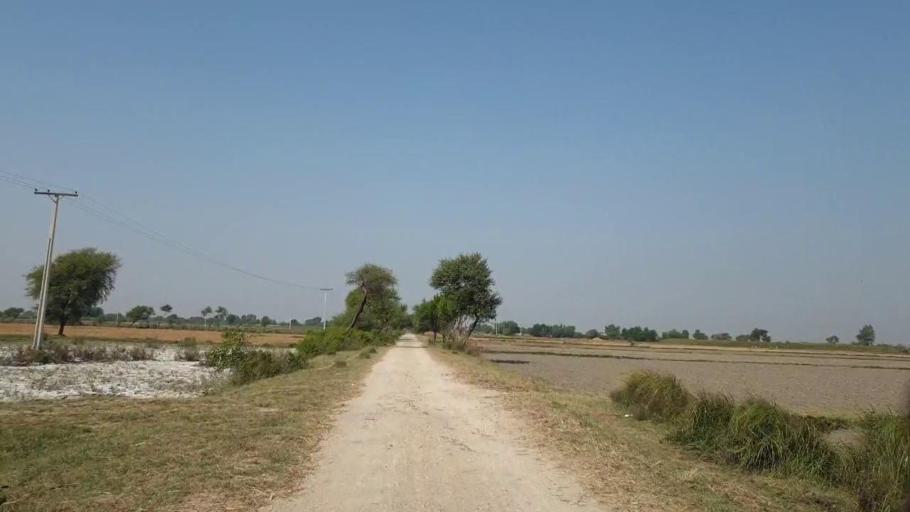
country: PK
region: Sindh
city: Tando Muhammad Khan
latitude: 25.0301
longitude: 68.4061
